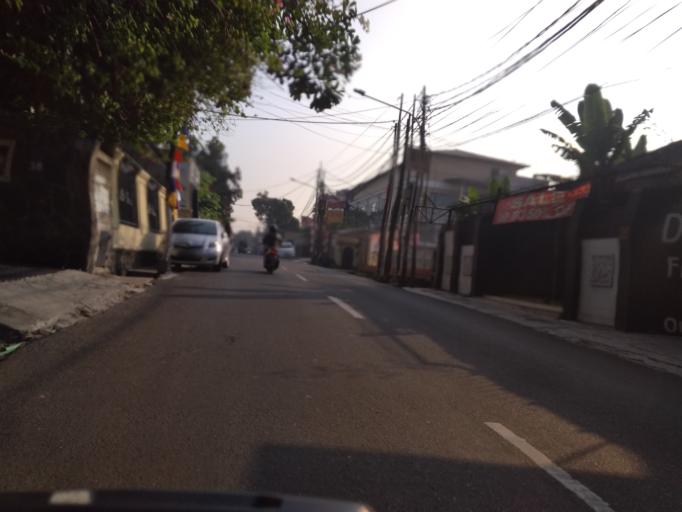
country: ID
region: Jakarta Raya
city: Jakarta
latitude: -6.2790
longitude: 106.8157
